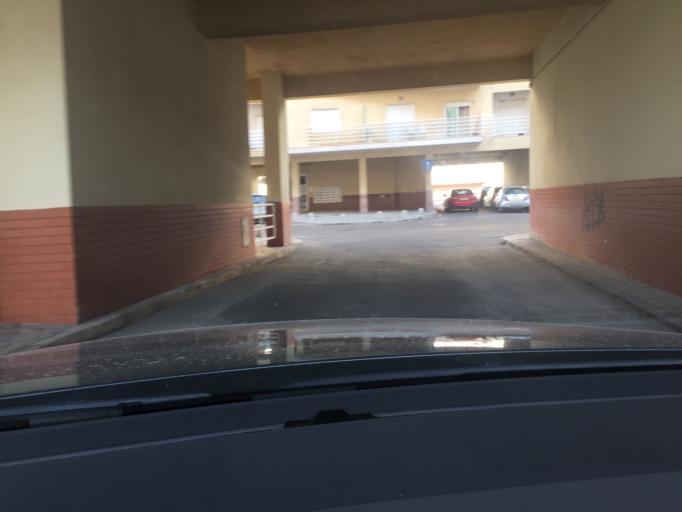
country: PT
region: Setubal
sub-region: Setubal
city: Setubal
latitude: 38.5322
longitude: -8.8862
